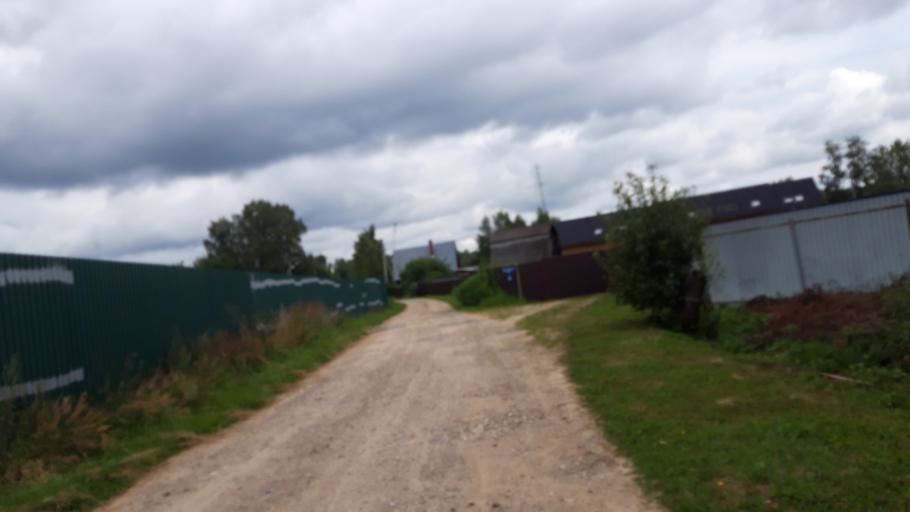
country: RU
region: Tverskaya
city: Konakovo
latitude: 56.6756
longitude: 36.7207
